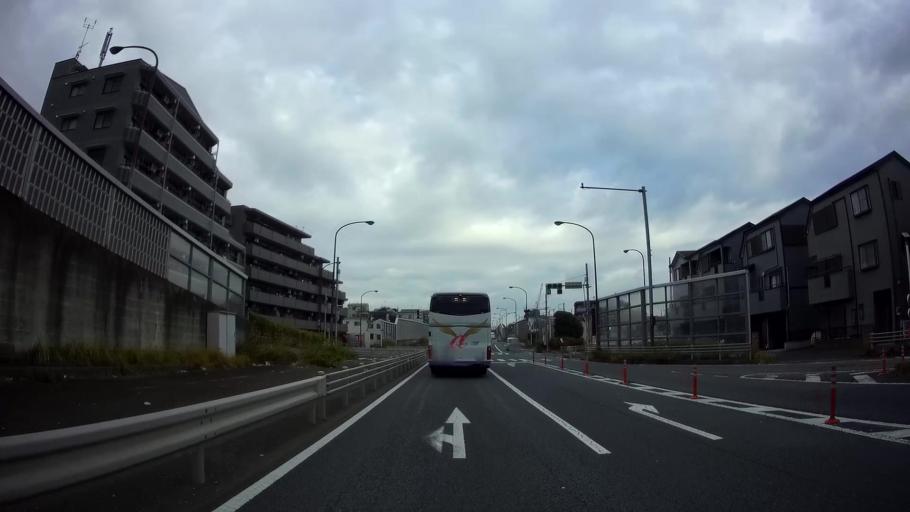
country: JP
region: Saitama
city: Wako
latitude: 35.7727
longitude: 139.6511
